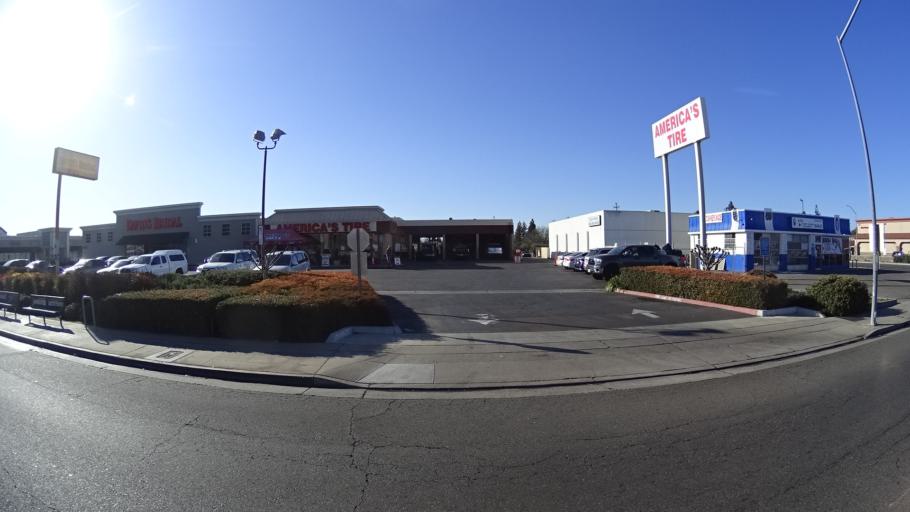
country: US
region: California
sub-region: Fresno County
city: Fresno
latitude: 36.8085
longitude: -119.7807
